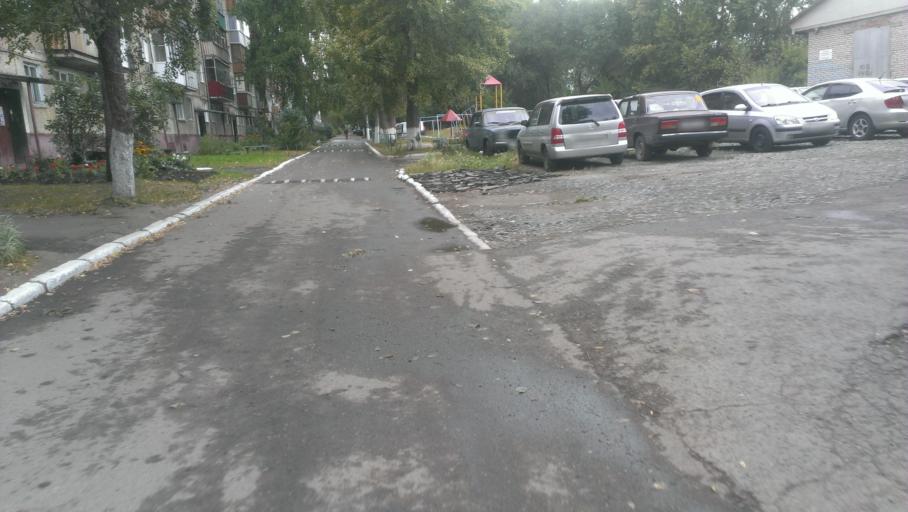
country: RU
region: Altai Krai
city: Novosilikatnyy
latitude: 53.3725
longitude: 83.6749
